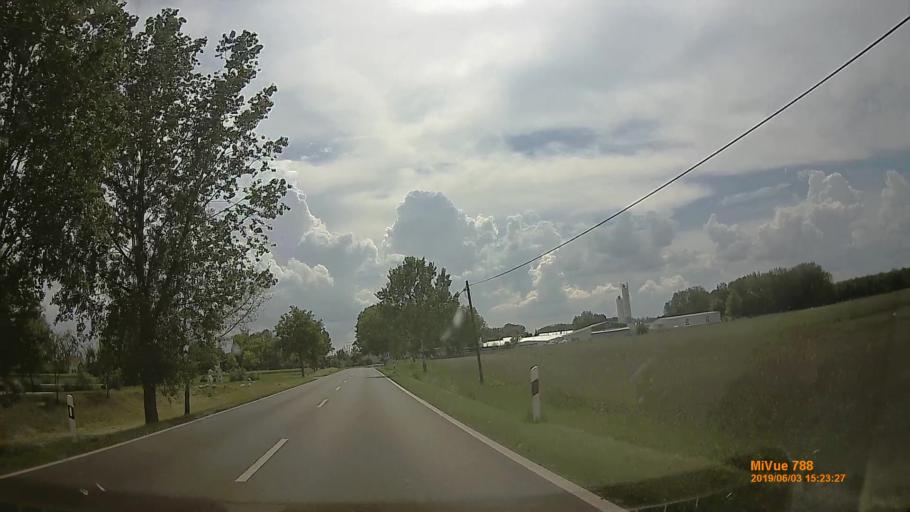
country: HU
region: Bacs-Kiskun
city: Tazlar
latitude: 46.6199
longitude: 19.4867
